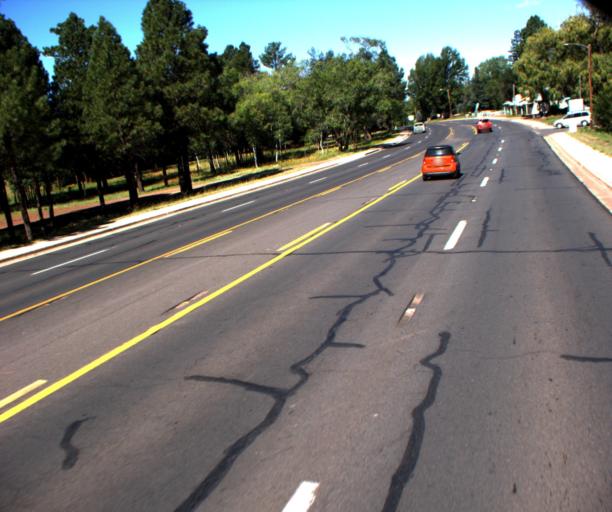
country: US
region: Arizona
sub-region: Navajo County
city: Pinetop-Lakeside
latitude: 34.1254
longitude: -109.9296
